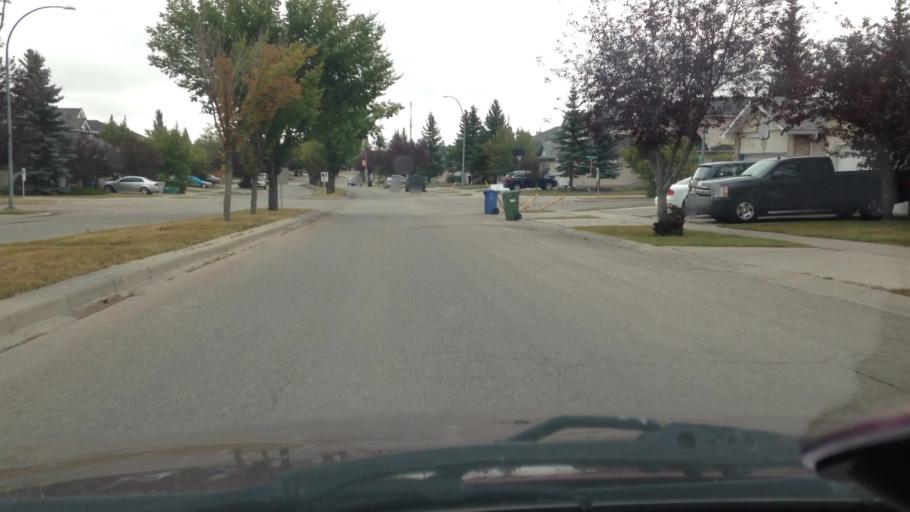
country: CA
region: Alberta
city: Calgary
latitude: 51.1470
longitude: -114.1134
